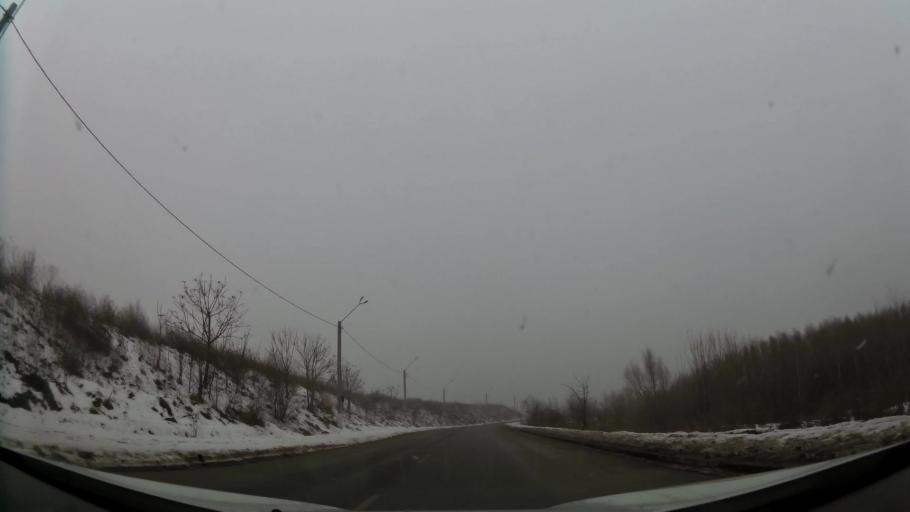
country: RO
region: Ilfov
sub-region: Comuna Chiajna
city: Rosu
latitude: 44.4600
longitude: 25.9939
